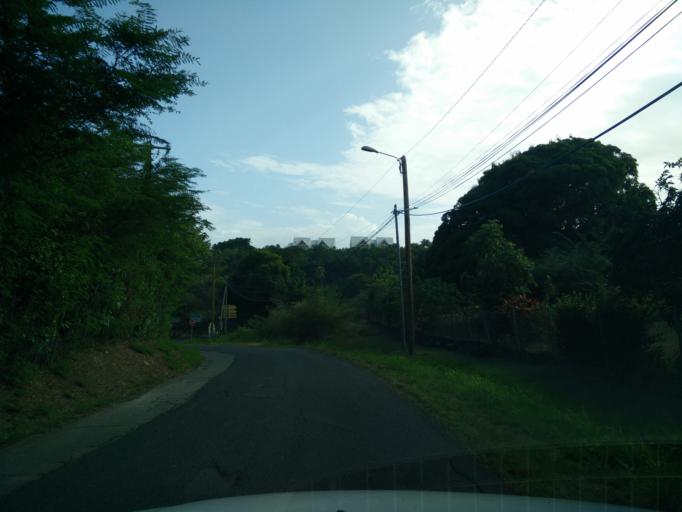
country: GP
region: Guadeloupe
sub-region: Guadeloupe
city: Sainte-Anne
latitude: 16.2397
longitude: -61.3786
